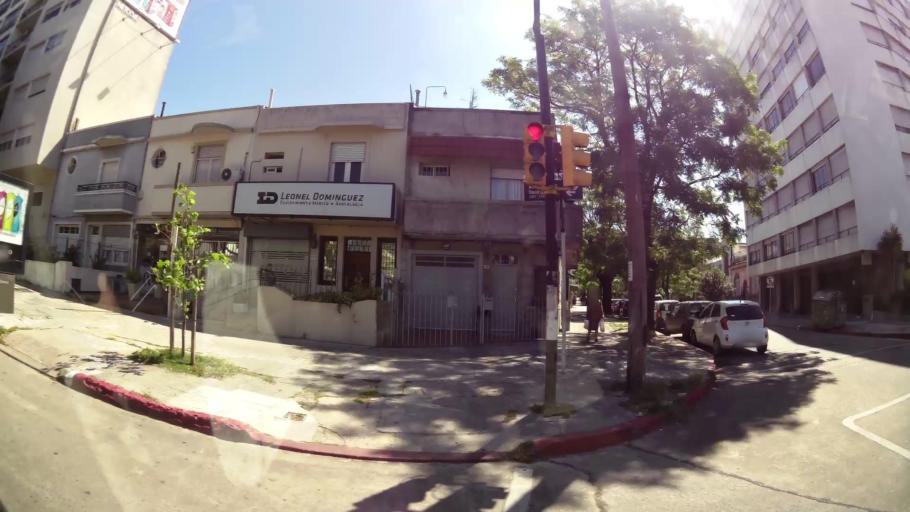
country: UY
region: Montevideo
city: Montevideo
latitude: -34.9062
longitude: -56.1548
